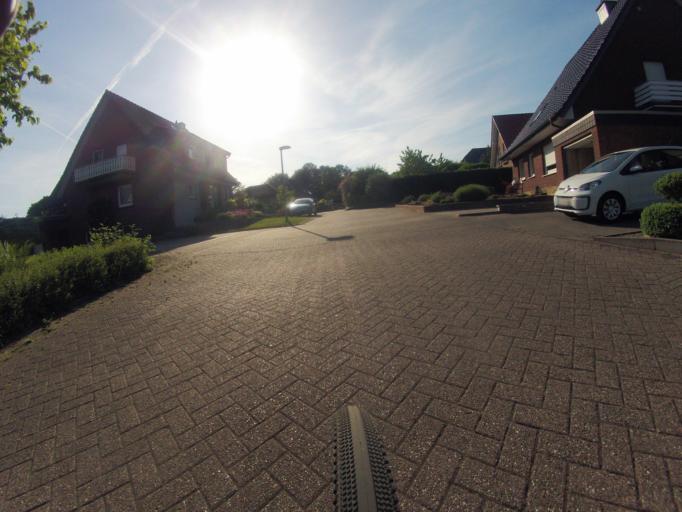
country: DE
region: North Rhine-Westphalia
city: Ibbenburen
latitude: 52.2936
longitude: 7.7023
